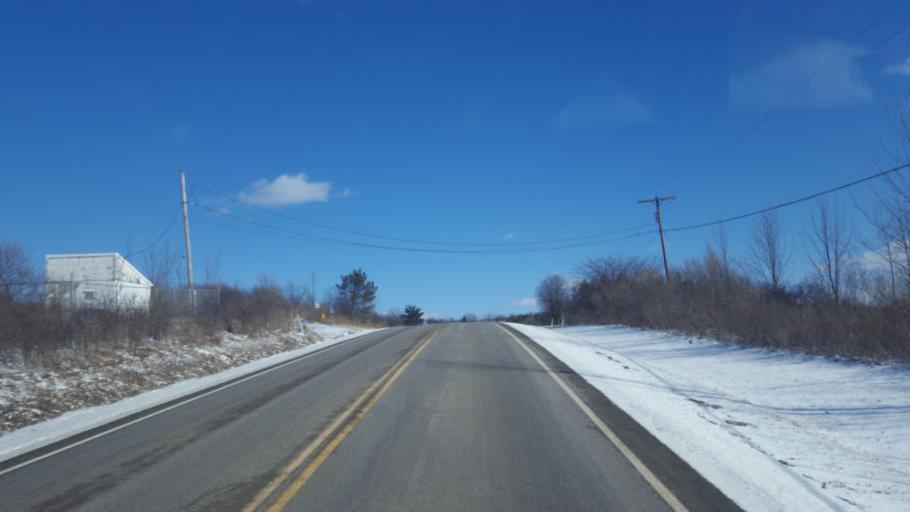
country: US
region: New York
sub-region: Allegany County
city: Friendship
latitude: 42.2019
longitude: -78.1125
